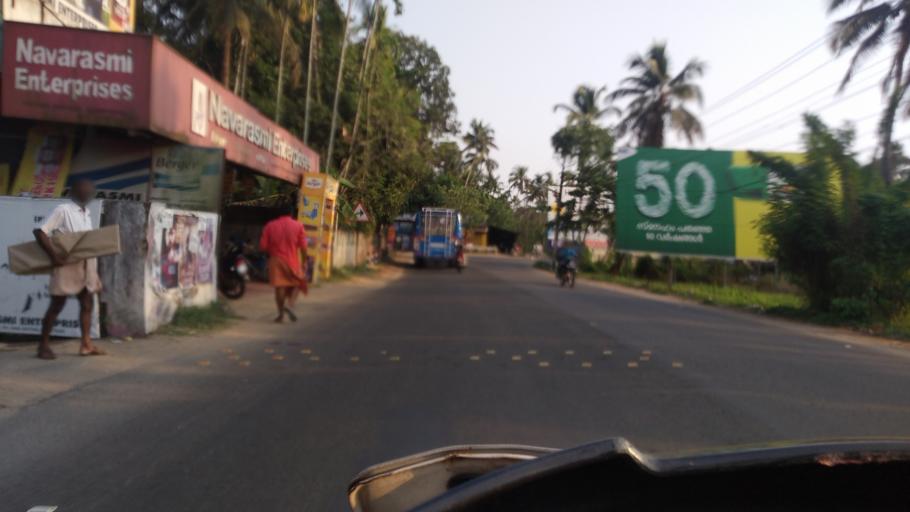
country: IN
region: Kerala
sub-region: Thrissur District
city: Thanniyam
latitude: 10.3687
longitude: 76.1249
